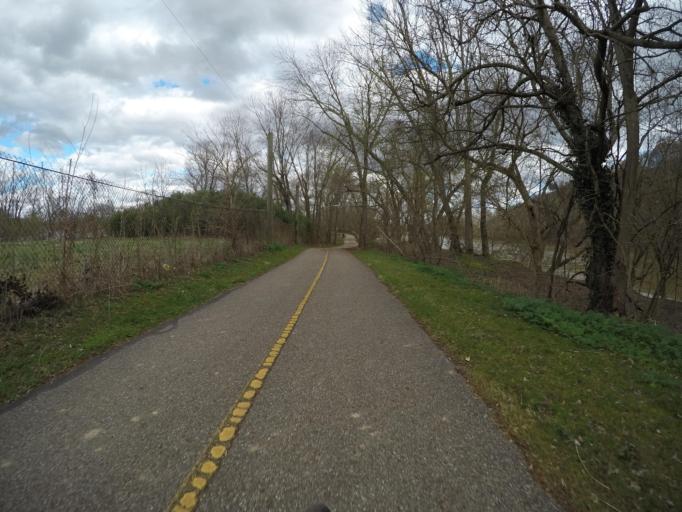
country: US
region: Ohio
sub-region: Washington County
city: Marietta
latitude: 39.4241
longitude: -81.4701
